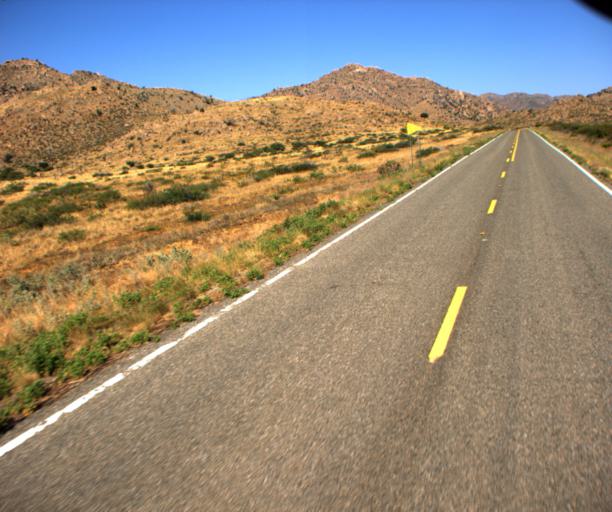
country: US
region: Arizona
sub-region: Graham County
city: Swift Trail Junction
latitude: 32.5607
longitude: -109.7736
